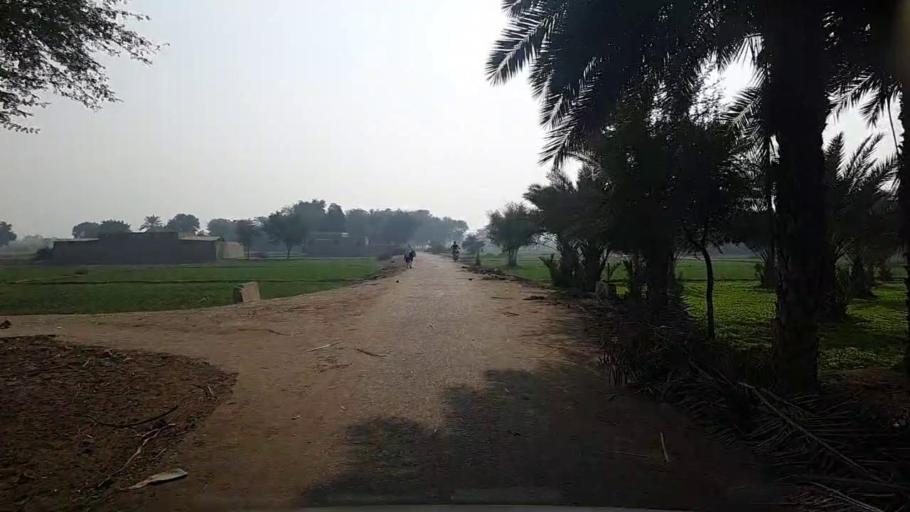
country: PK
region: Sindh
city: Setharja Old
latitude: 27.1192
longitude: 68.5161
